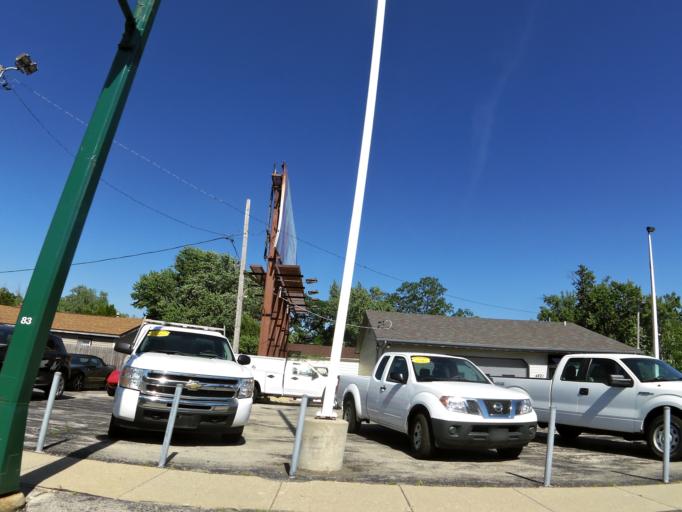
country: US
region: Illinois
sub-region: Winnebago County
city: Loves Park
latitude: 42.3005
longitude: -89.0576
